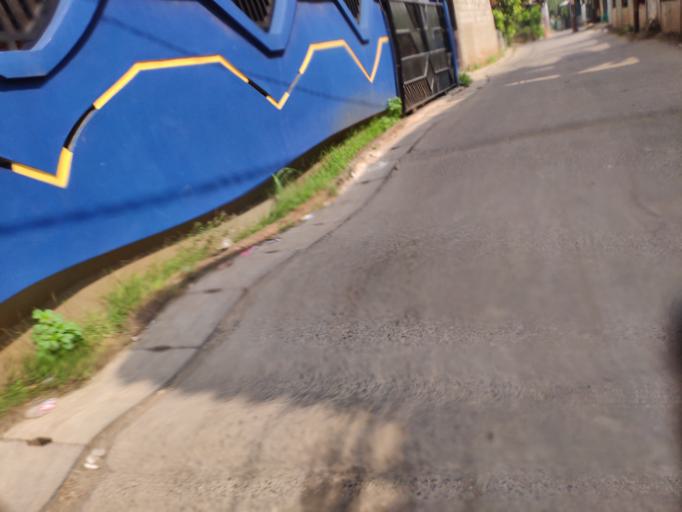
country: ID
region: West Java
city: Pamulang
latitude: -6.3312
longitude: 106.7994
